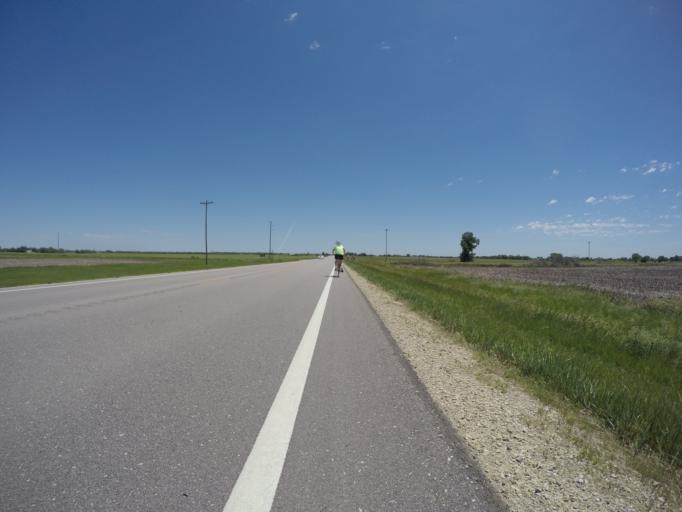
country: US
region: Kansas
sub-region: Republic County
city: Belleville
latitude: 39.8127
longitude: -97.6719
